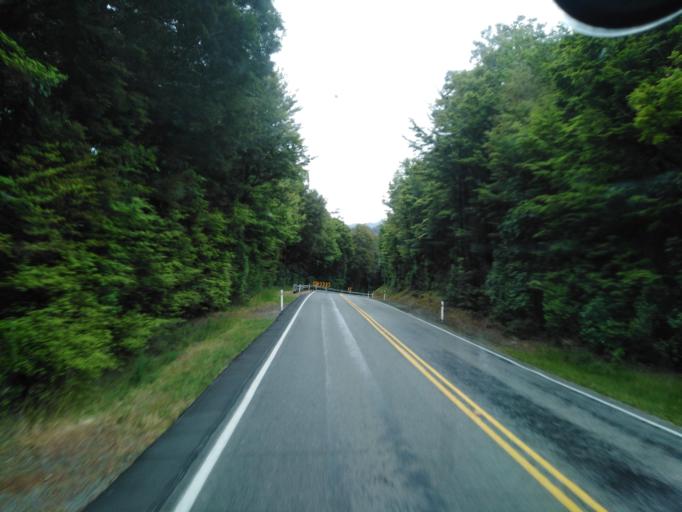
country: NZ
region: Tasman
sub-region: Tasman District
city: Wakefield
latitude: -41.7101
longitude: 172.5793
